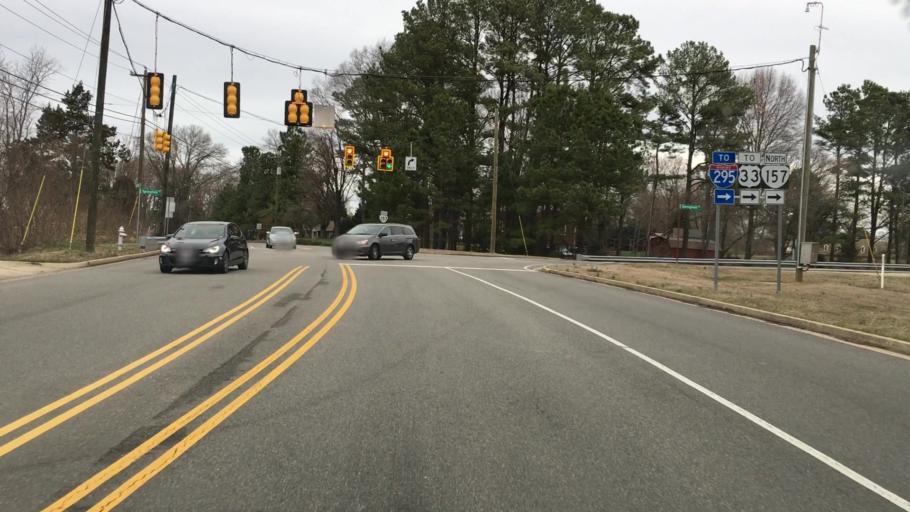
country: US
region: Virginia
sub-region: Henrico County
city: Glen Allen
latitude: 37.6710
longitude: -77.5418
